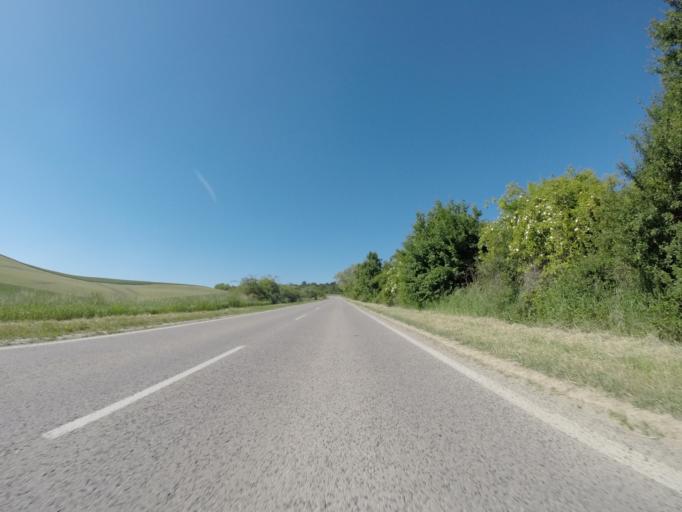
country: SK
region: Trnavsky
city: Hlohovec
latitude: 48.3457
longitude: 17.7844
